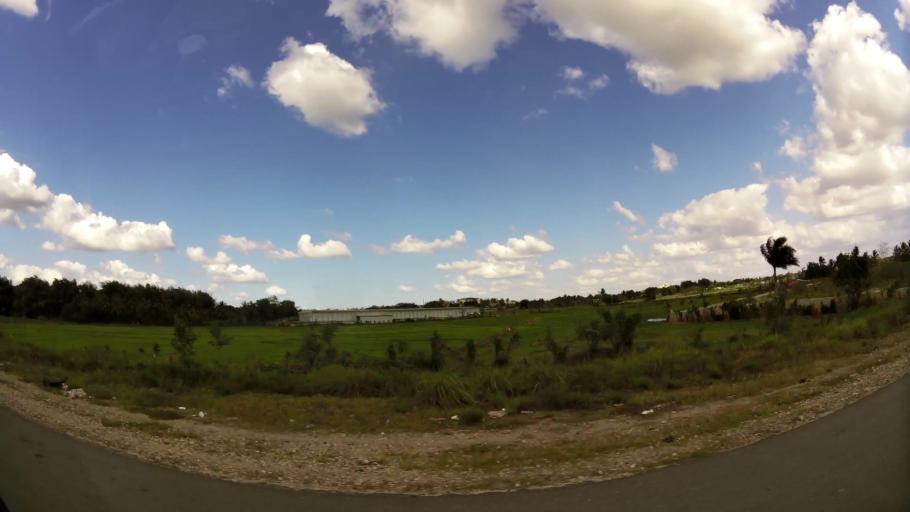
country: DO
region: Santo Domingo
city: Santo Domingo Oeste
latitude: 18.5249
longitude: -70.0659
